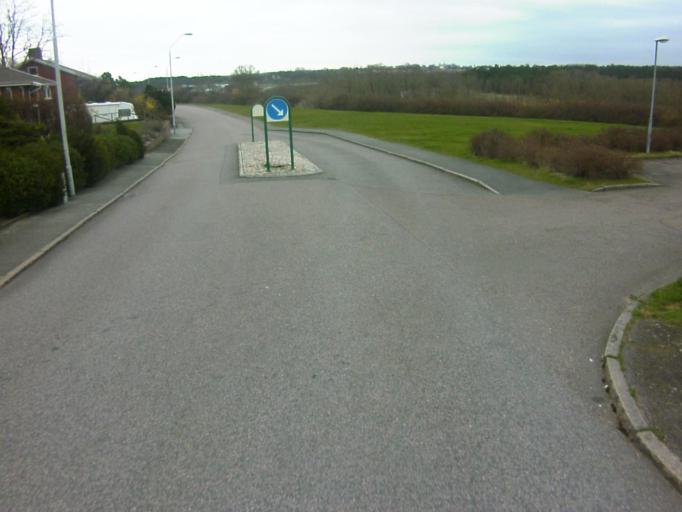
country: SE
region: Skane
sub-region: Kavlinge Kommun
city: Kaevlinge
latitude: 55.7885
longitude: 13.0896
